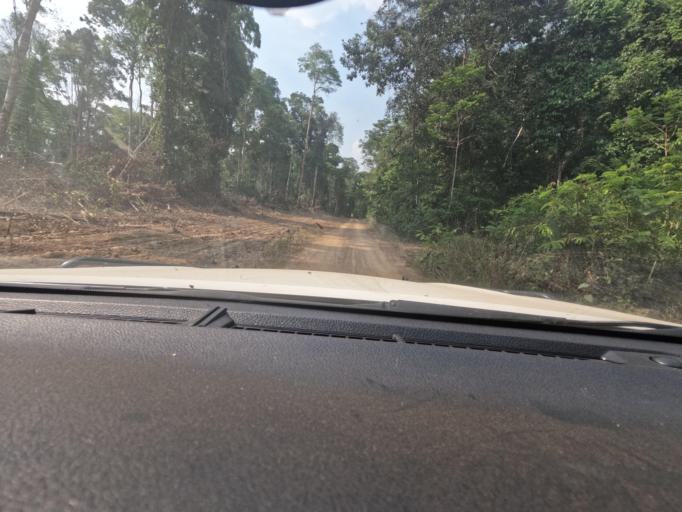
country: BR
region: Rondonia
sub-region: Porto Velho
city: Porto Velho
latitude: -8.6678
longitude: -63.1558
